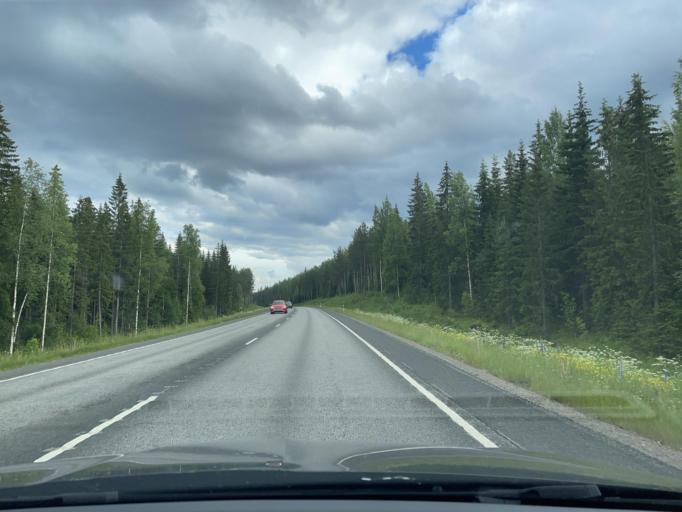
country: FI
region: Central Finland
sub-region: Jyvaeskylae
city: Jyvaeskylae
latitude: 62.2406
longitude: 25.6566
